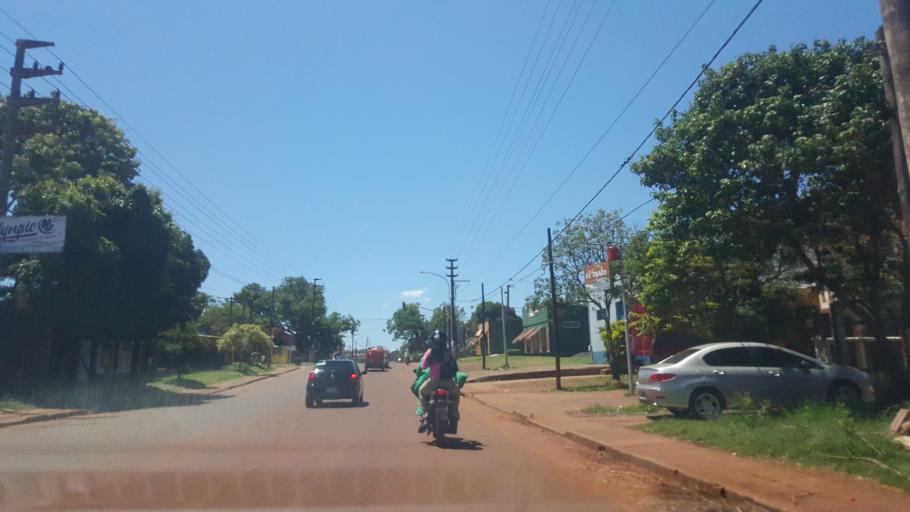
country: AR
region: Misiones
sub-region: Departamento de Capital
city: Posadas
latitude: -27.4105
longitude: -55.9119
